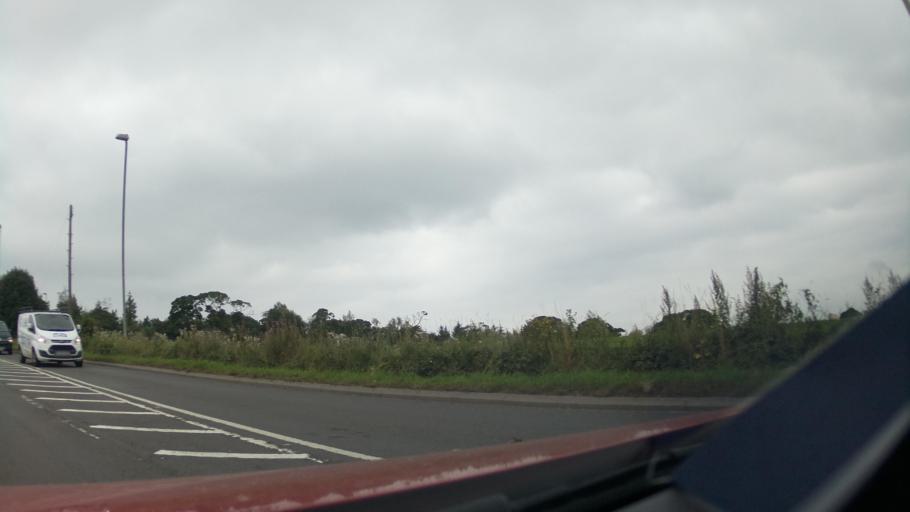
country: GB
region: England
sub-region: Staffordshire
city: Cheddleton
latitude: 53.0214
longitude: -2.0404
